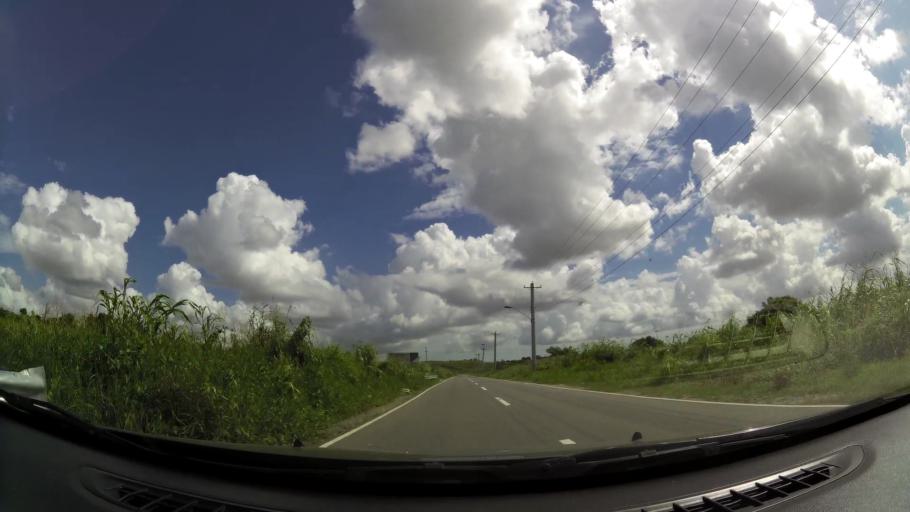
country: TT
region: Penal/Debe
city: Debe
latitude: 10.2335
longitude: -61.4946
